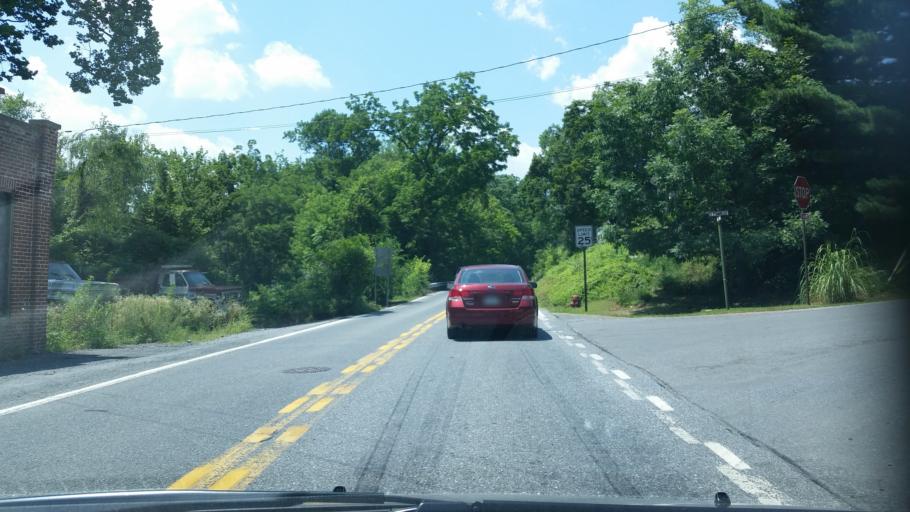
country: US
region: Pennsylvania
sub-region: Dauphin County
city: Hummelstown
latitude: 40.2885
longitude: -76.6845
